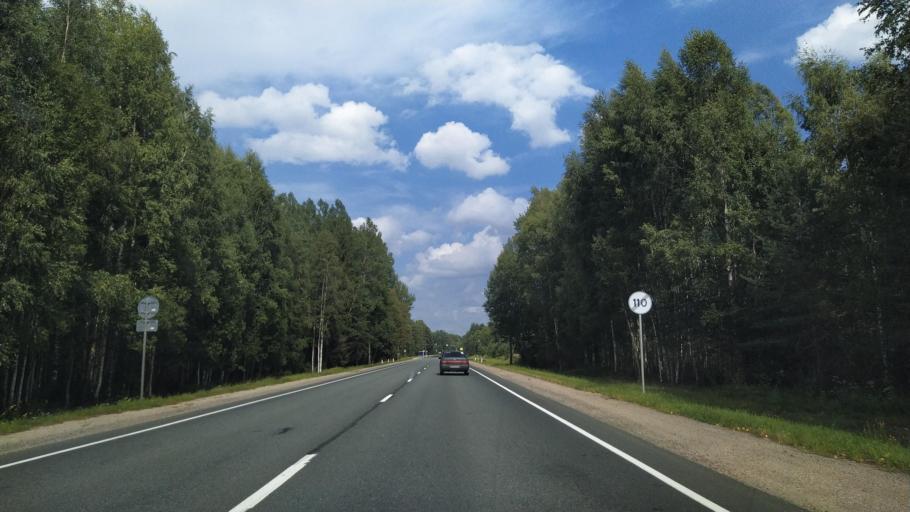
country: RU
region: Pskov
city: Porkhov
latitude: 57.8600
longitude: 29.5690
